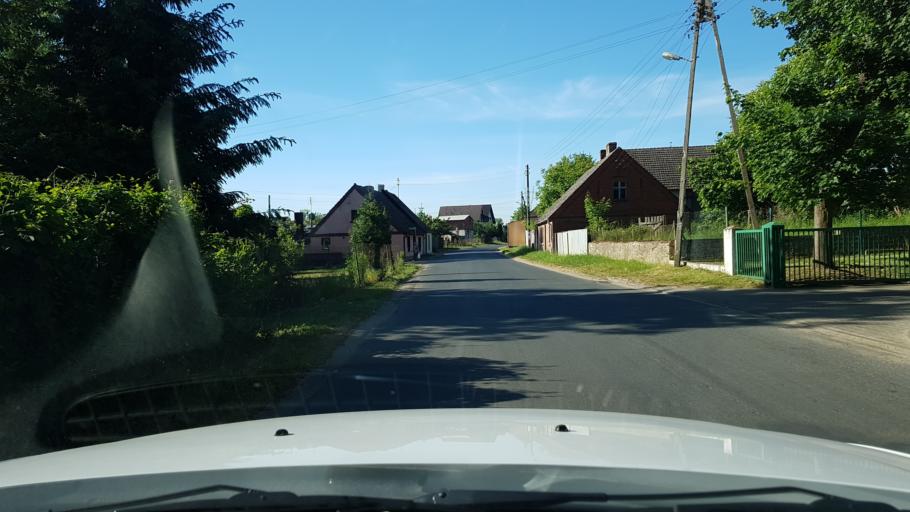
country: PL
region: West Pomeranian Voivodeship
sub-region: Powiat pyrzycki
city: Bielice
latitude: 53.2195
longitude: 14.6099
